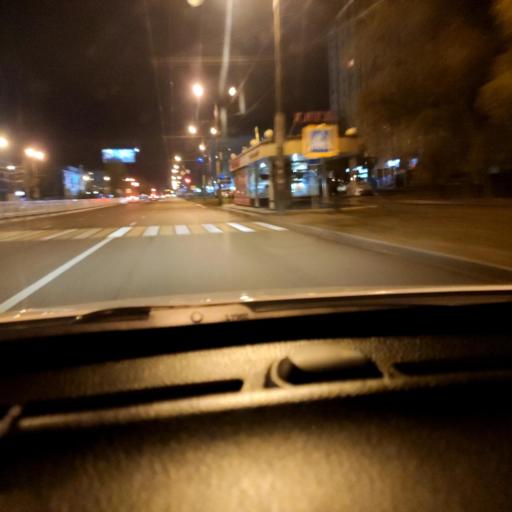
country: RU
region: Voronezj
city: Podgornoye
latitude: 51.7124
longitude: 39.1651
